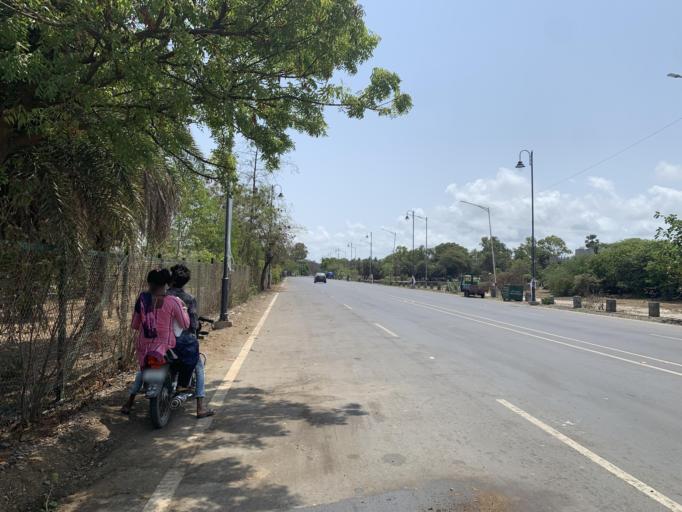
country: IN
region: Daman and Diu
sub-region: Daman District
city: Daman
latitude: 20.4575
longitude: 72.8433
